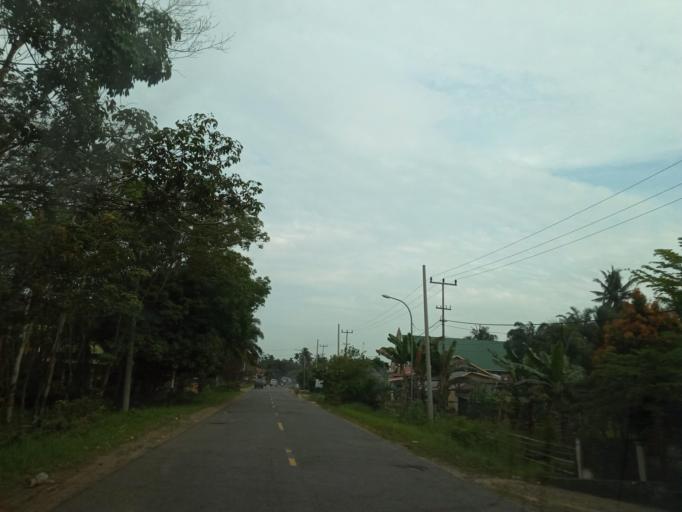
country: ID
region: Jambi
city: Muara Tembesi
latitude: -1.7172
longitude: 103.1245
